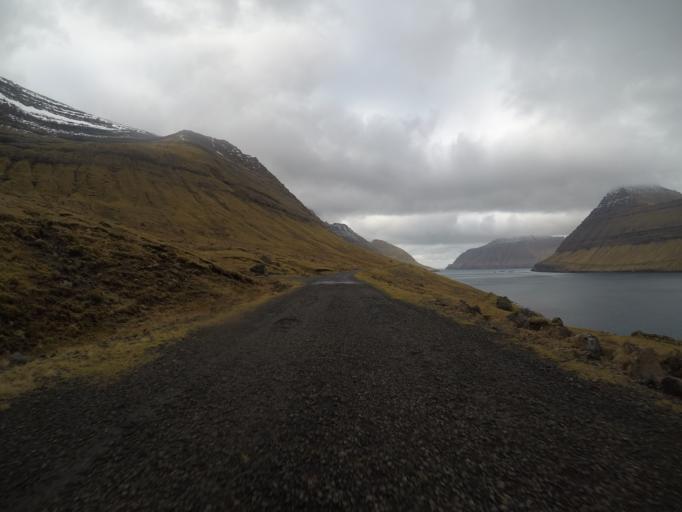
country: FO
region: Nordoyar
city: Klaksvik
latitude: 62.3174
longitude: -6.5567
